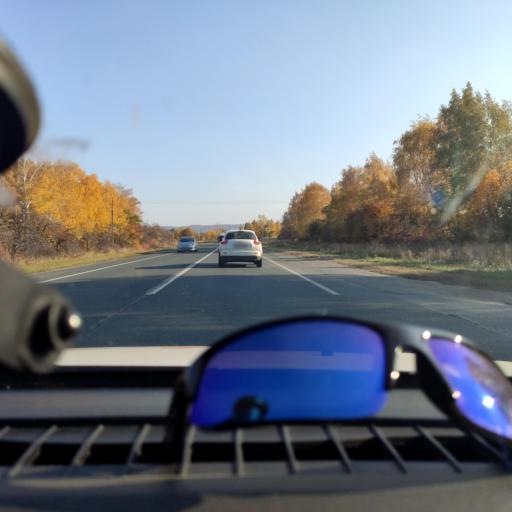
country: RU
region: Samara
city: Volzhskiy
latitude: 53.4683
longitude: 50.1255
